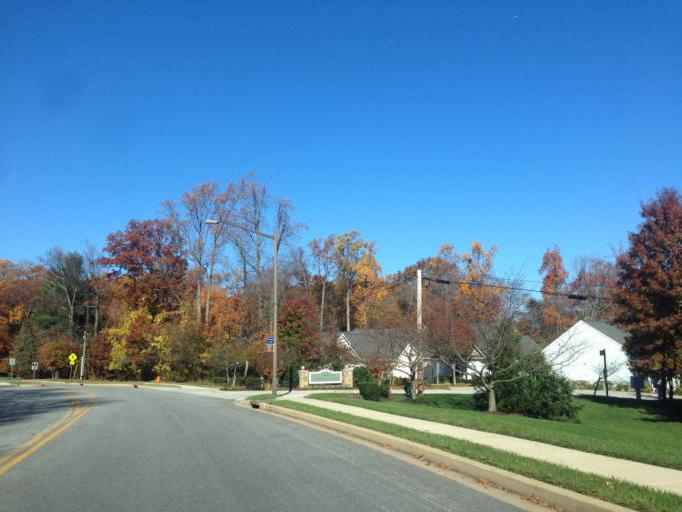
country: US
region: Maryland
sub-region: Howard County
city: Riverside
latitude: 39.1953
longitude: -76.8811
